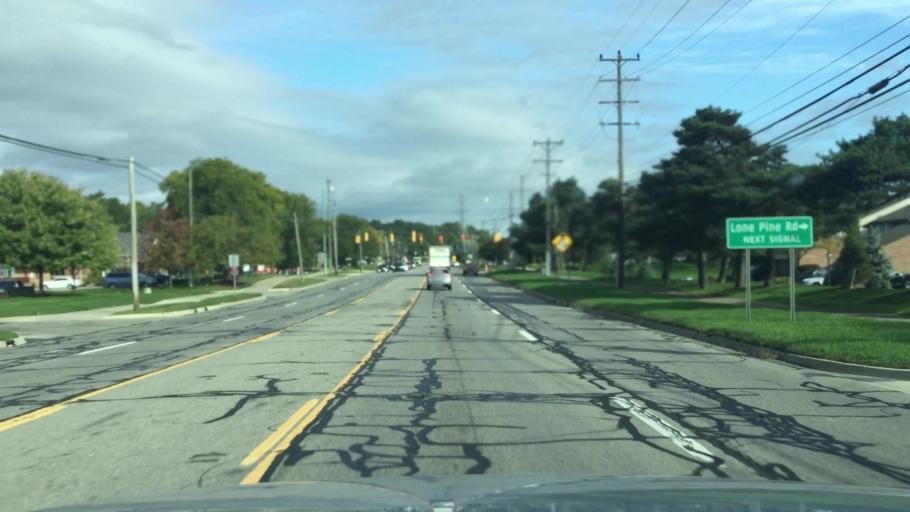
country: US
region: Michigan
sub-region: Oakland County
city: Orchard Lake
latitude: 42.5721
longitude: -83.3620
